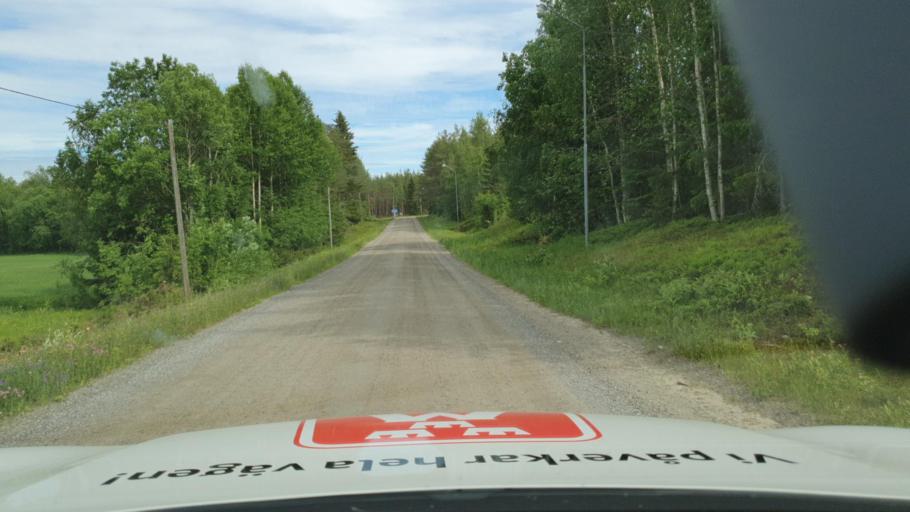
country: SE
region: Vaesterbotten
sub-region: Skelleftea Kommun
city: Burea
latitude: 64.3711
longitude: 21.0804
